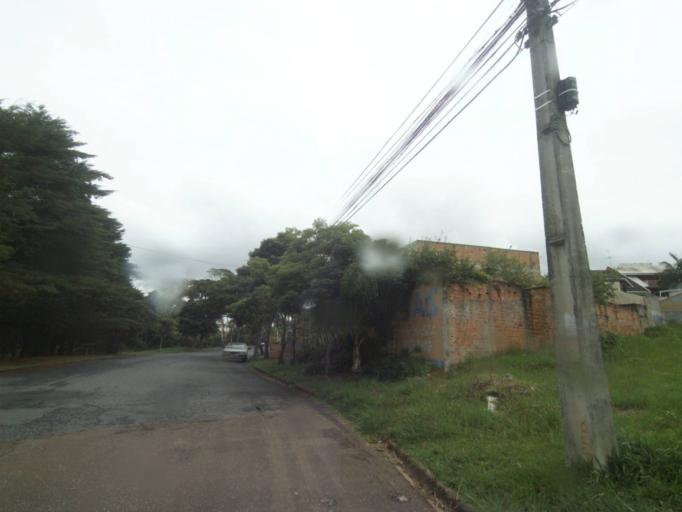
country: BR
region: Parana
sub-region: Curitiba
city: Curitiba
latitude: -25.4498
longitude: -49.3440
